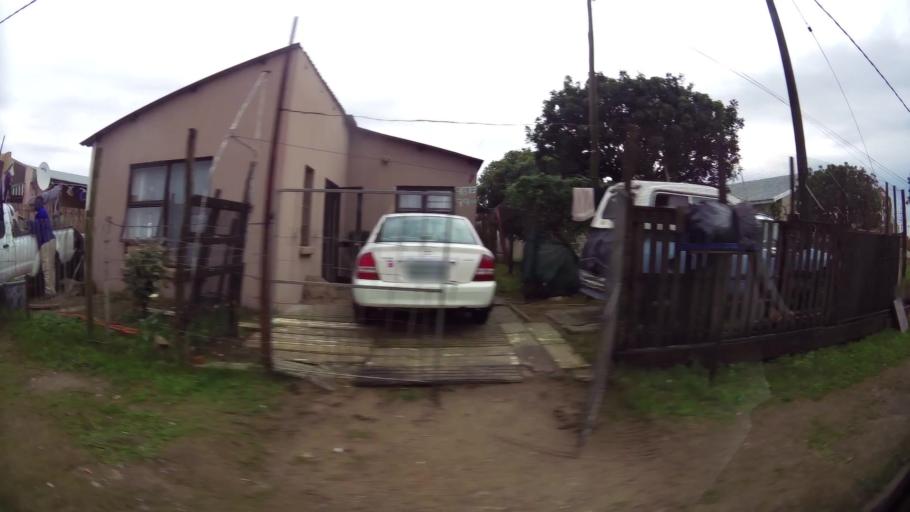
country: ZA
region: Eastern Cape
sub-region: Nelson Mandela Bay Metropolitan Municipality
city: Port Elizabeth
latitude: -33.9908
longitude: 25.5864
